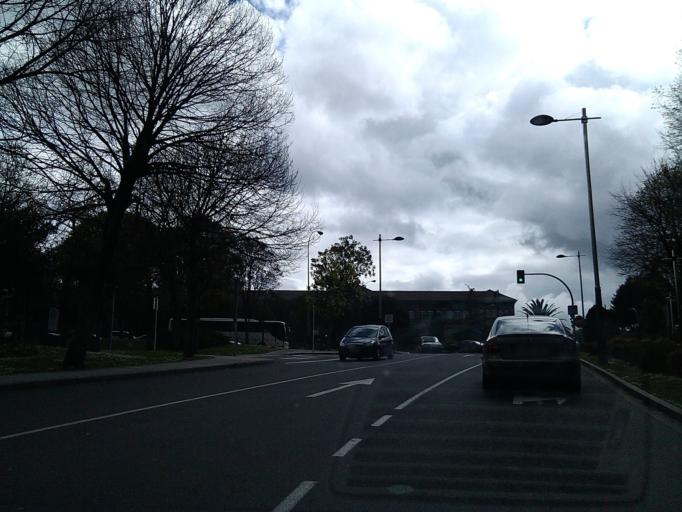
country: ES
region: Galicia
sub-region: Provincia da Coruna
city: Santiago de Compostela
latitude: 42.8894
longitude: -8.5366
